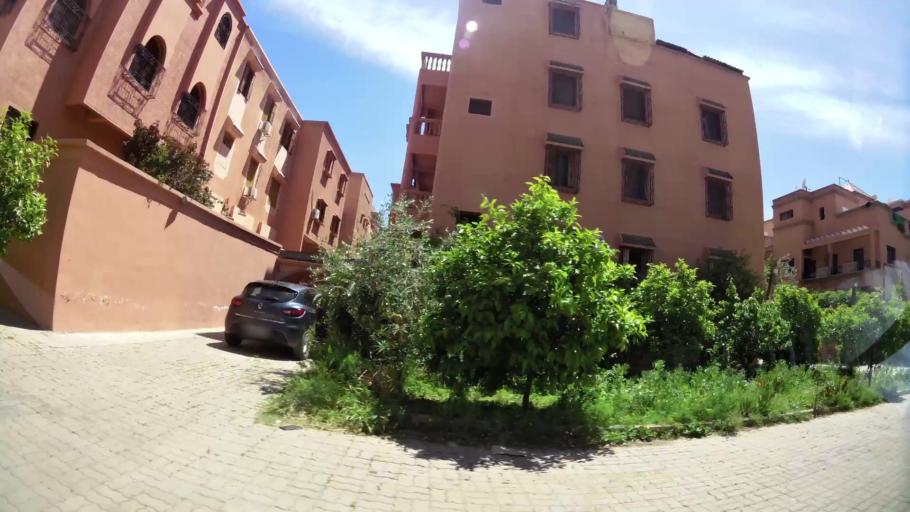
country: MA
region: Marrakech-Tensift-Al Haouz
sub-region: Marrakech
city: Marrakesh
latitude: 31.6414
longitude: -8.0624
